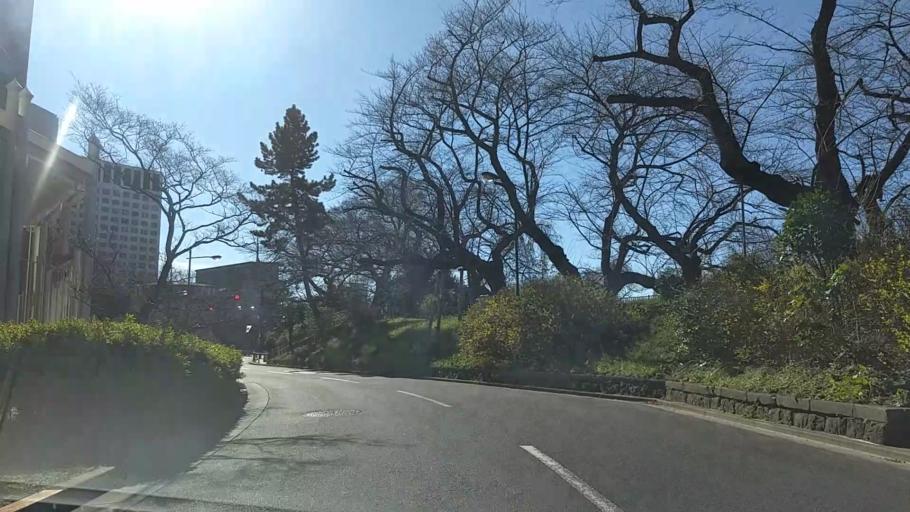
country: JP
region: Tokyo
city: Tokyo
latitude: 35.6870
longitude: 139.7314
